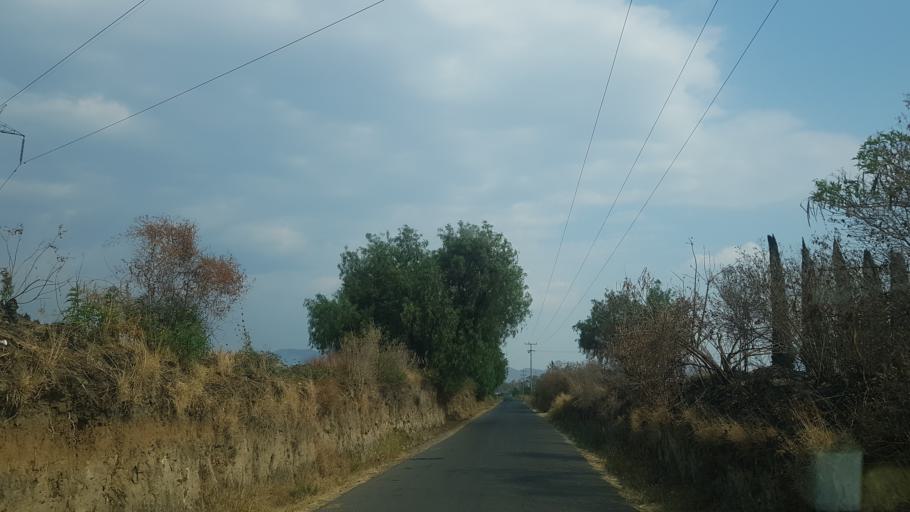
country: MX
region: Puebla
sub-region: Santa Isabel Cholula
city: Santa Ana Acozautla
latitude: 18.9529
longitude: -98.3986
